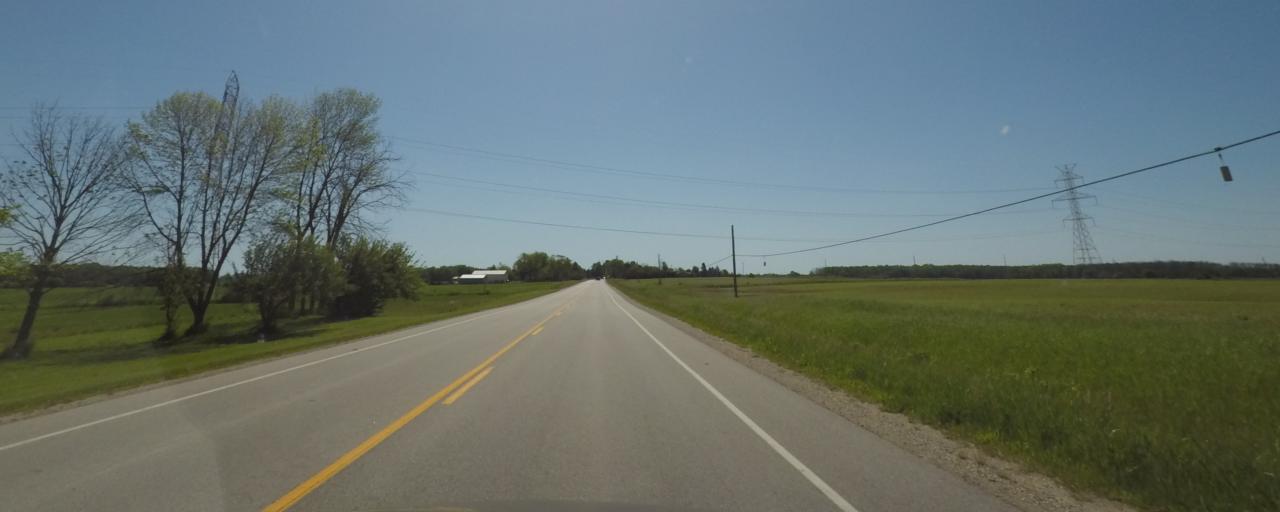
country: US
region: Wisconsin
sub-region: Sheboygan County
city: Sheboygan Falls
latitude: 43.7444
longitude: -87.8774
